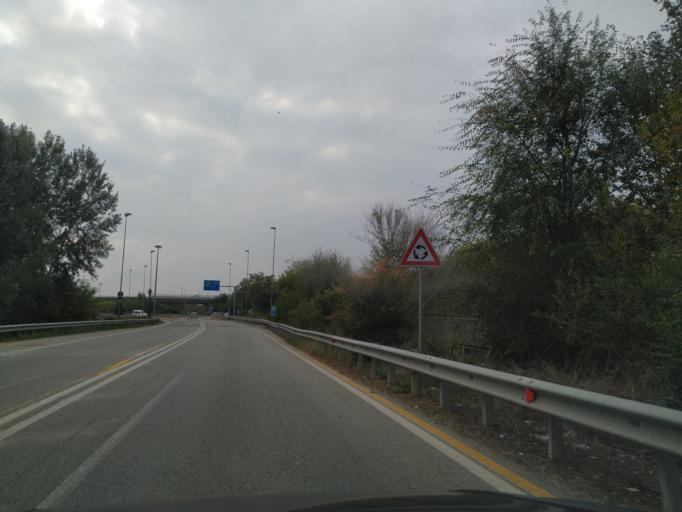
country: IT
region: Piedmont
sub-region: Provincia di Torino
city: Brandizzo
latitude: 45.1888
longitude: 7.8614
